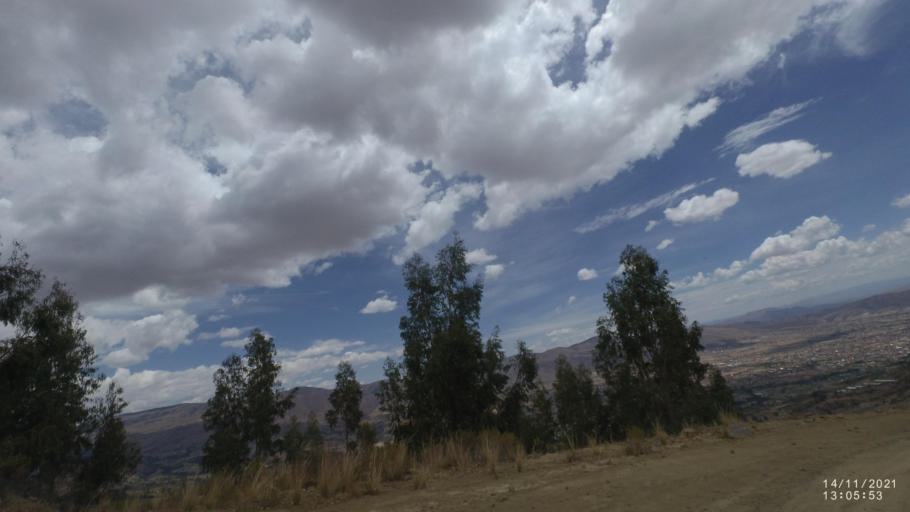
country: BO
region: Cochabamba
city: Colomi
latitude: -17.3727
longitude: -65.9805
